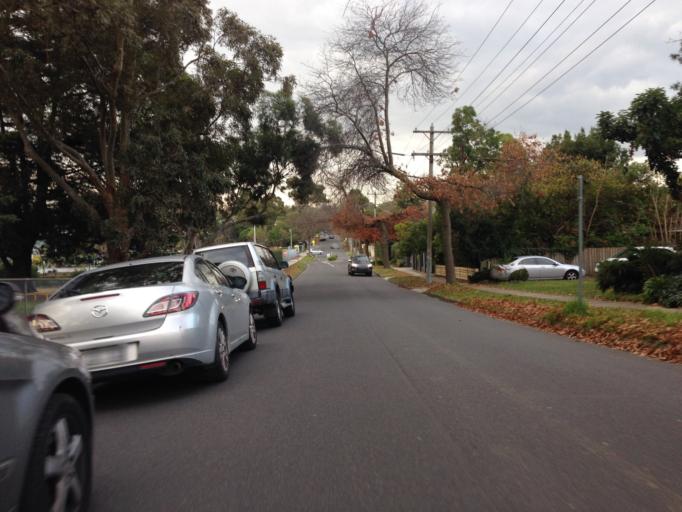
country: AU
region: Victoria
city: Balwyn
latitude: -37.8008
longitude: 145.0765
